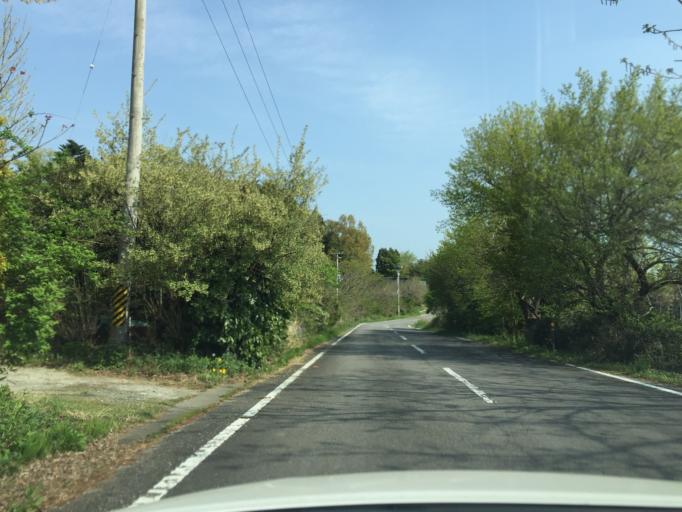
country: JP
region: Fukushima
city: Iwaki
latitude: 37.1572
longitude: 140.8550
